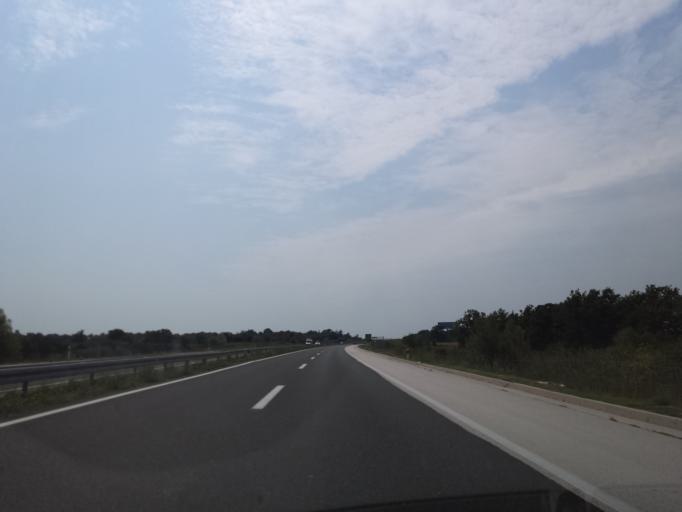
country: HR
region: Zadarska
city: Posedarje
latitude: 44.1991
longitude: 15.4420
